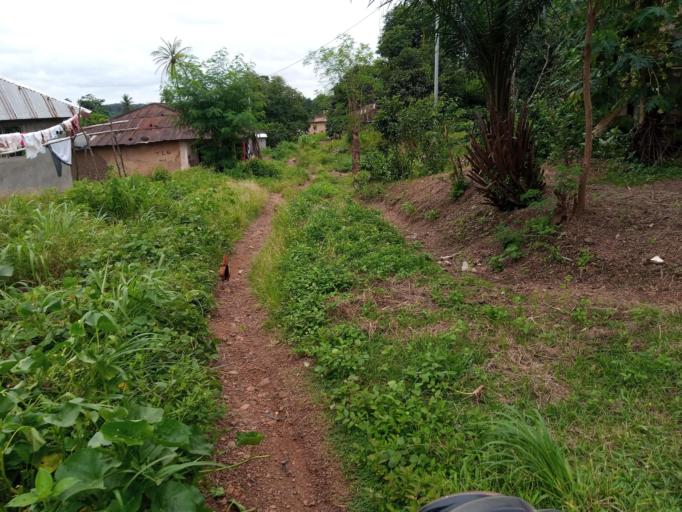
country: SL
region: Southern Province
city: Largo
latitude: 8.2036
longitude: -12.0588
